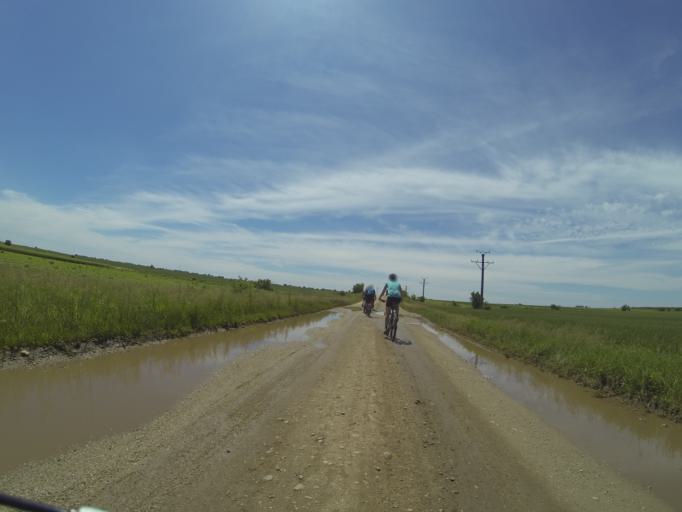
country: RO
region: Dolj
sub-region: Comuna Leu
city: Zanoaga
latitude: 44.1730
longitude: 24.0919
